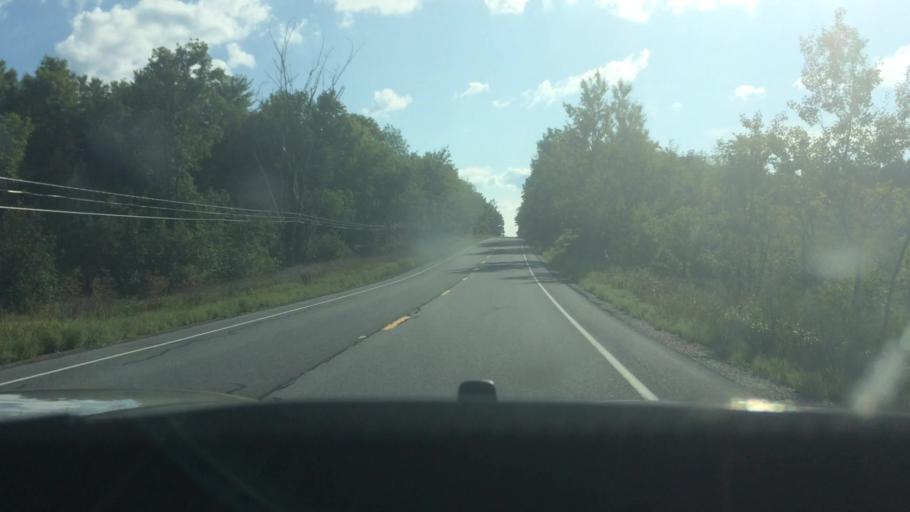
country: US
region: New York
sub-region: Franklin County
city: Malone
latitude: 44.7408
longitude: -74.5821
